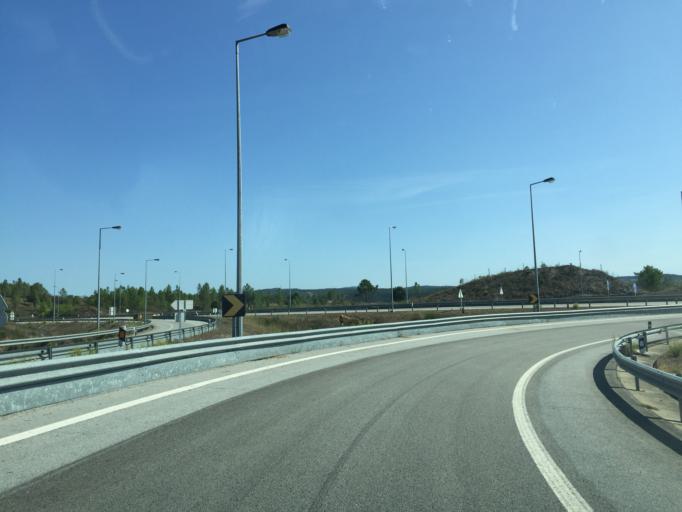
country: PT
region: Portalegre
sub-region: Nisa
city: Nisa
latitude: 39.5594
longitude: -7.8015
